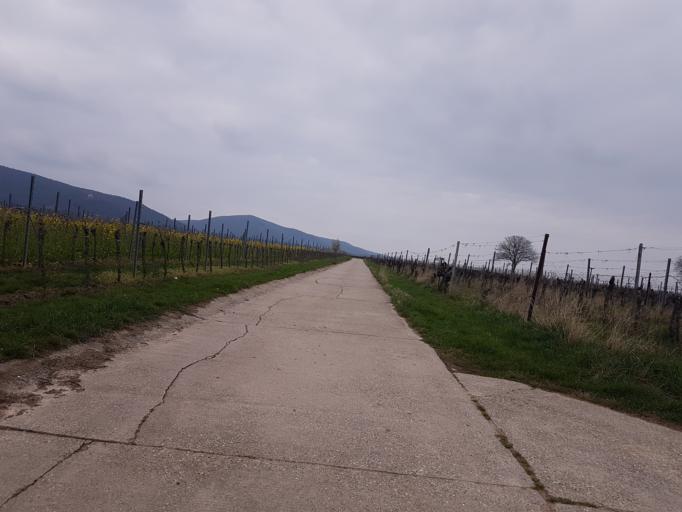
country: DE
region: Rheinland-Pfalz
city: Bochingen
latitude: 49.2310
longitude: 8.0797
